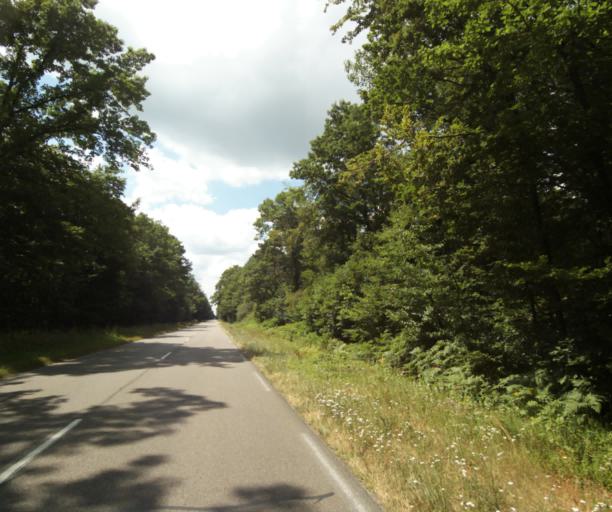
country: FR
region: Ile-de-France
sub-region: Departement de Seine-et-Marne
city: Thomery
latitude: 48.4200
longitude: 2.8095
